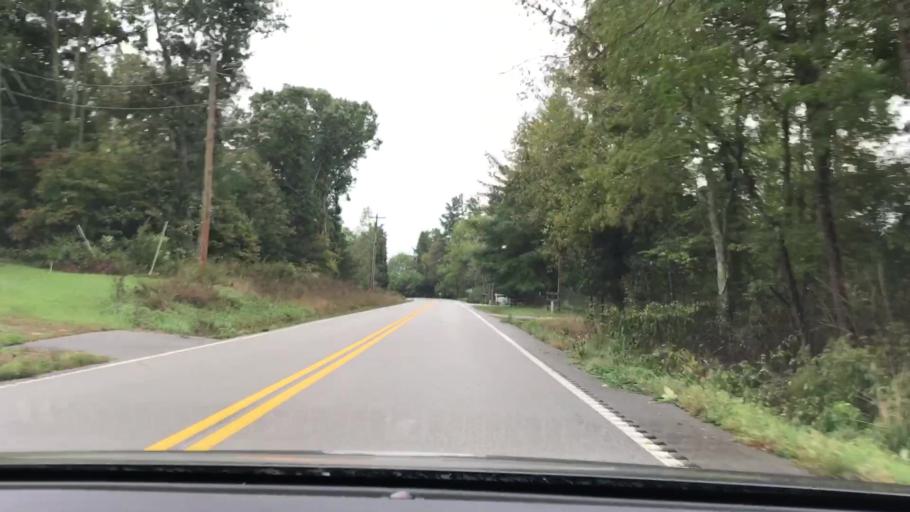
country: US
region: Tennessee
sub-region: Fentress County
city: Jamestown
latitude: 36.3690
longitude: -84.7591
